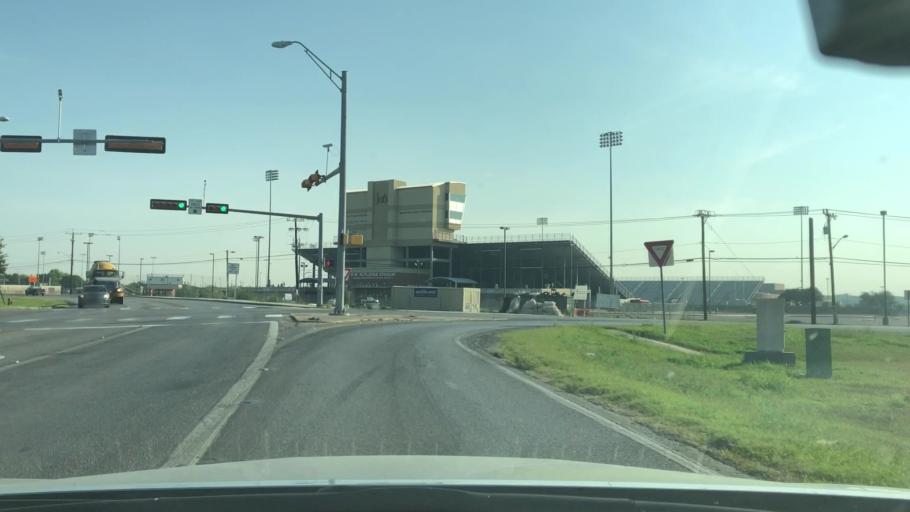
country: US
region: Texas
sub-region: Bexar County
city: Converse
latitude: 29.5086
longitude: -98.3060
